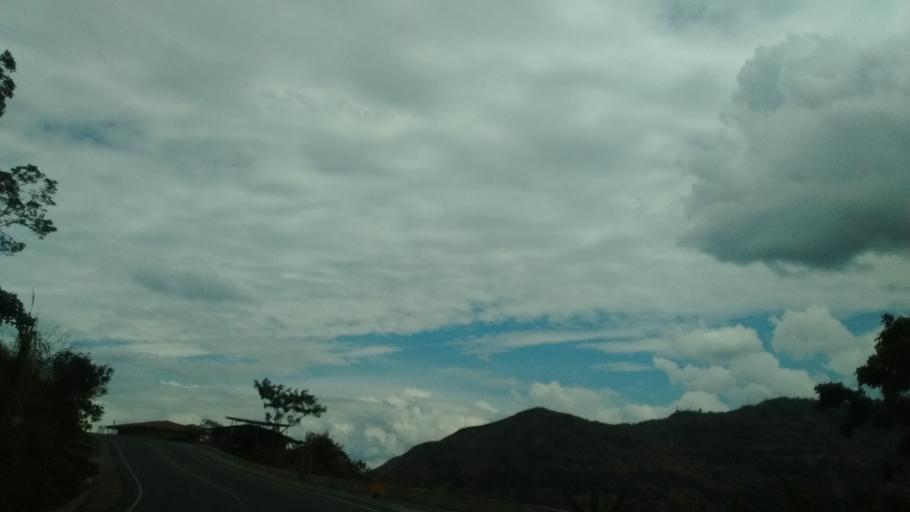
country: CO
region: Cauca
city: Rosas
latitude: 2.2815
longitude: -76.7155
